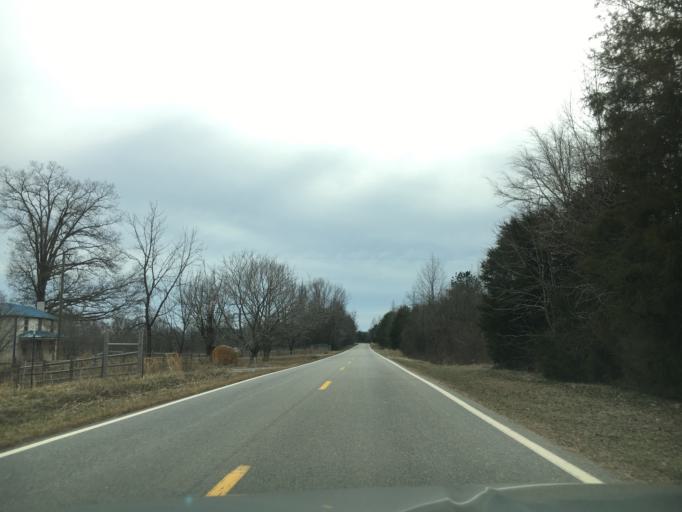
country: US
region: Virginia
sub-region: Charlotte County
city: Charlotte Court House
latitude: 37.1292
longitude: -78.7550
